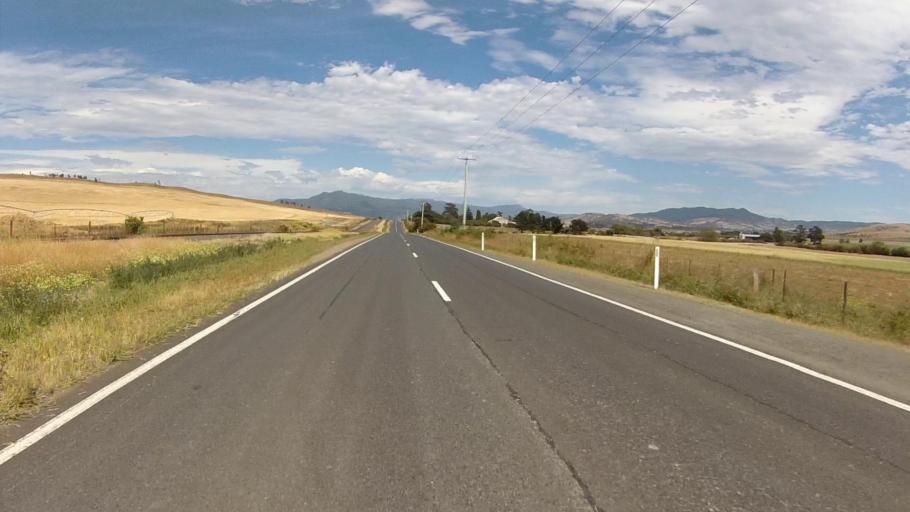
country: AU
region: Tasmania
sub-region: Brighton
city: Bridgewater
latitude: -42.6903
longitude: 147.3123
